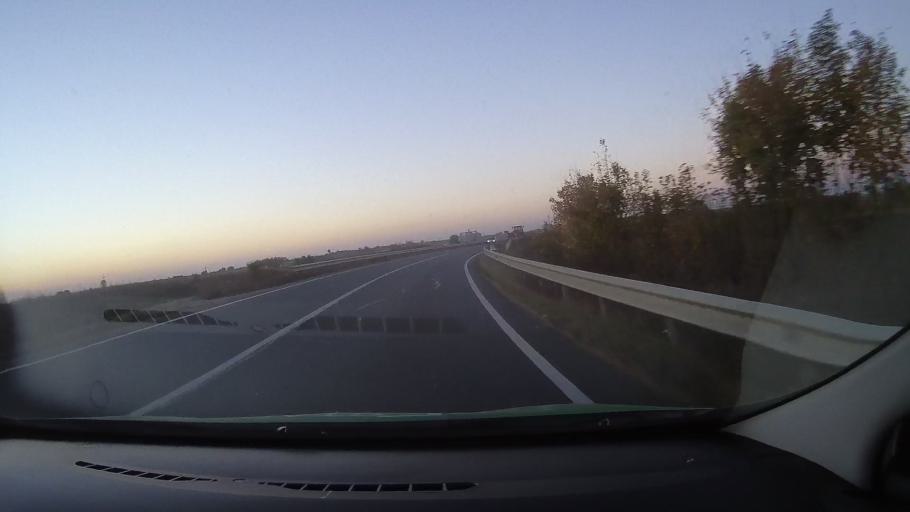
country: RO
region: Bihor
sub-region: Comuna Tarcea
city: Tarcea
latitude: 47.4472
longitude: 22.1860
